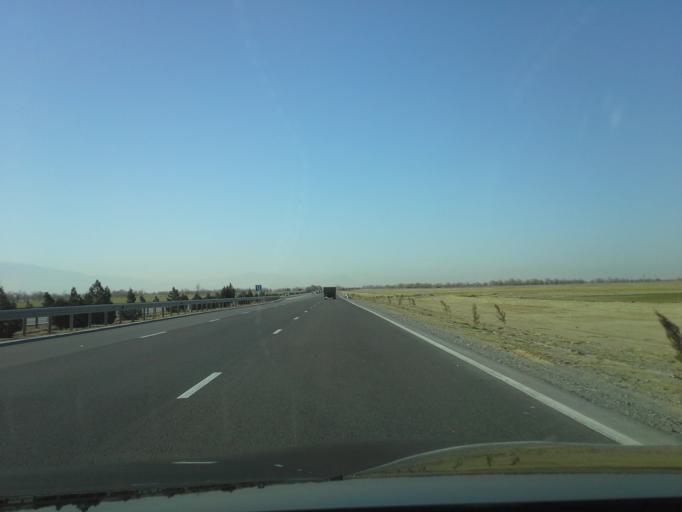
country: TM
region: Ahal
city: Annau
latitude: 37.8974
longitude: 58.5933
